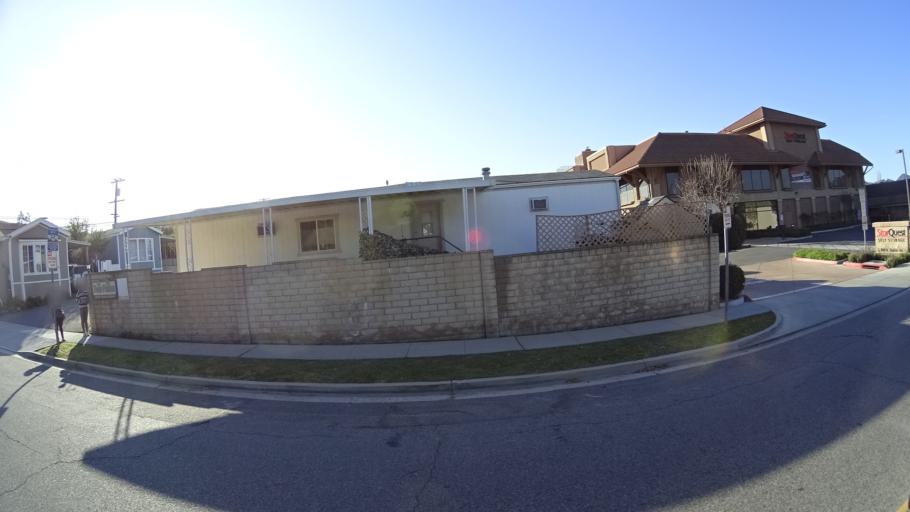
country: US
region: California
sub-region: Ventura County
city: Thousand Oaks
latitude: 34.1720
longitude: -118.8367
